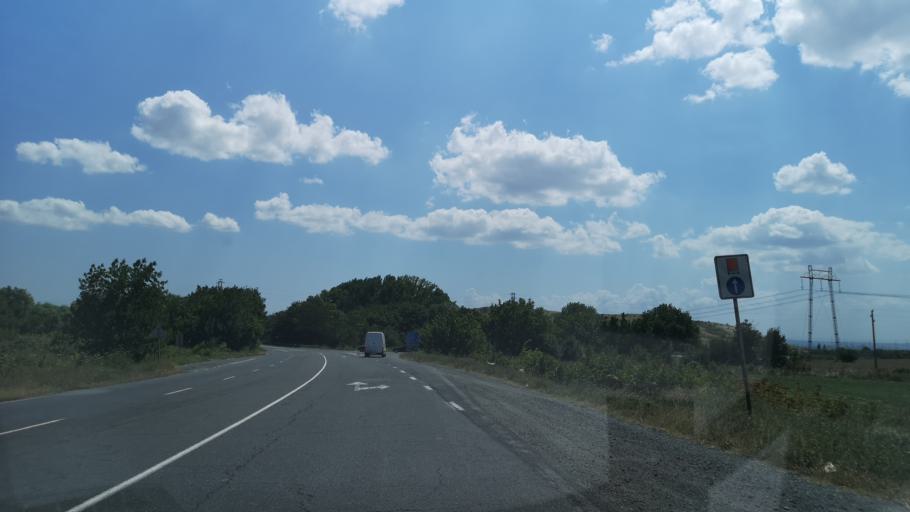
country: BG
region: Burgas
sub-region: Obshtina Kameno
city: Kameno
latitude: 42.6251
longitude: 27.3459
